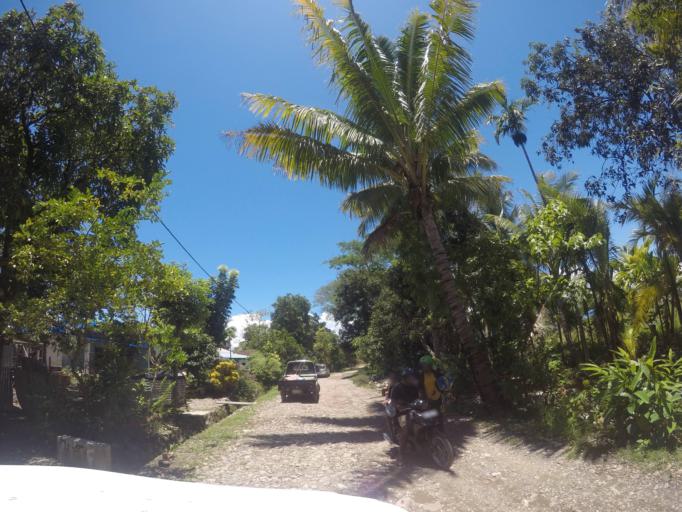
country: TL
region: Bobonaro
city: Maliana
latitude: -8.9876
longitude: 125.2167
